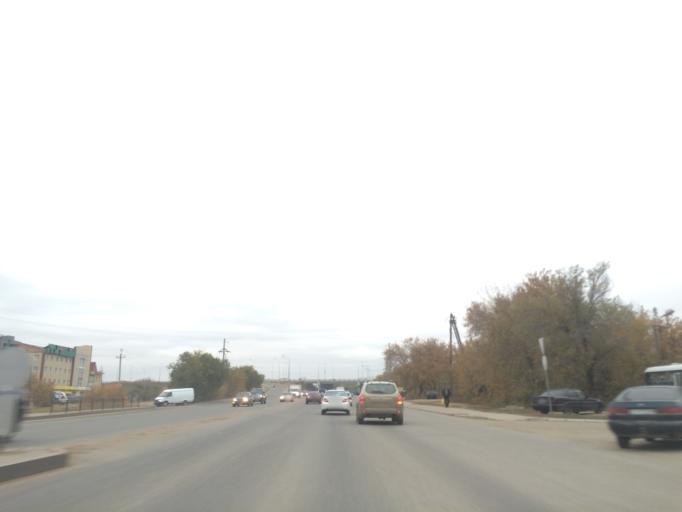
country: KZ
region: Astana Qalasy
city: Astana
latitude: 51.1842
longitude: 71.4525
